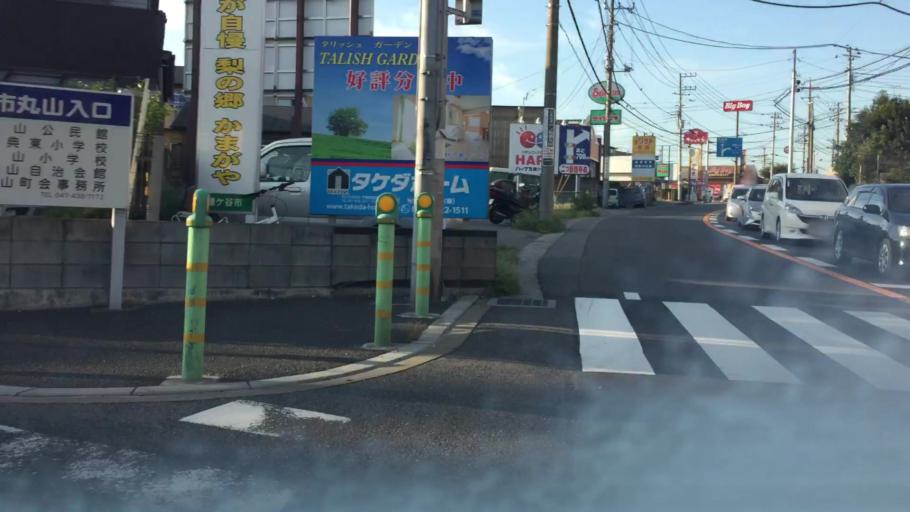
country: JP
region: Chiba
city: Funabashi
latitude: 35.7451
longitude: 139.9975
